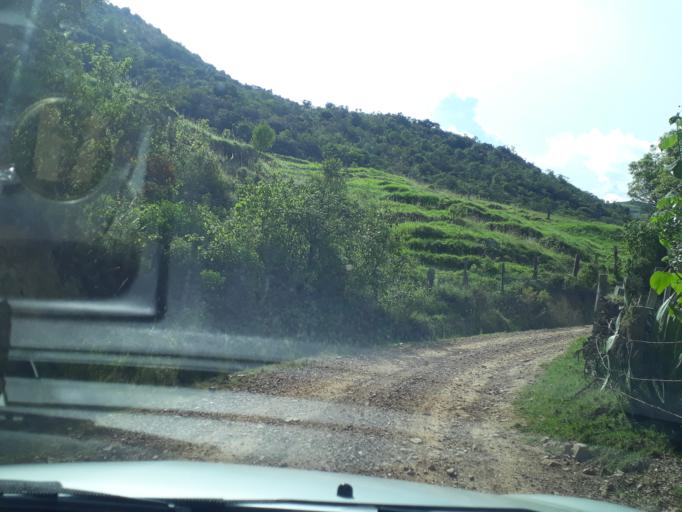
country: CO
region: Boyaca
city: Santa Rosa de Viterbo
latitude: 5.8520
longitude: -72.9666
